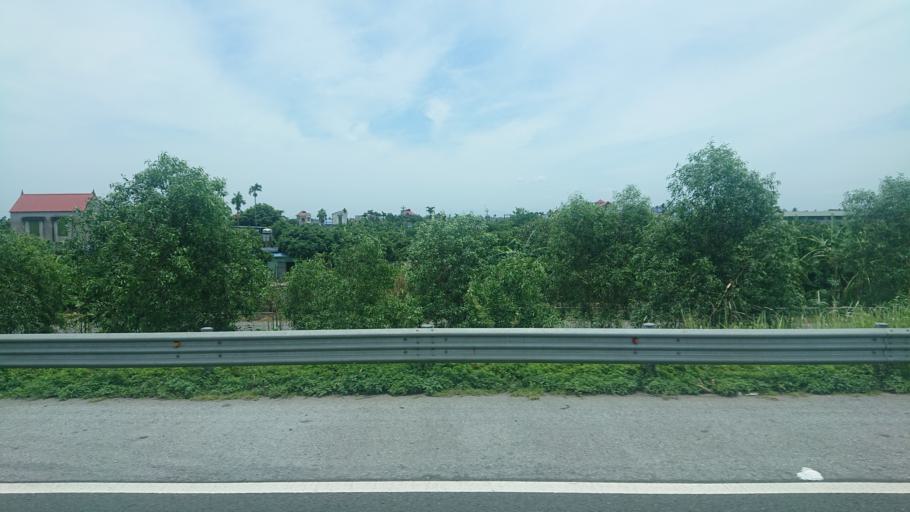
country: VN
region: Hai Duong
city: Tu Ky
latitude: 20.8298
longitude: 106.4513
